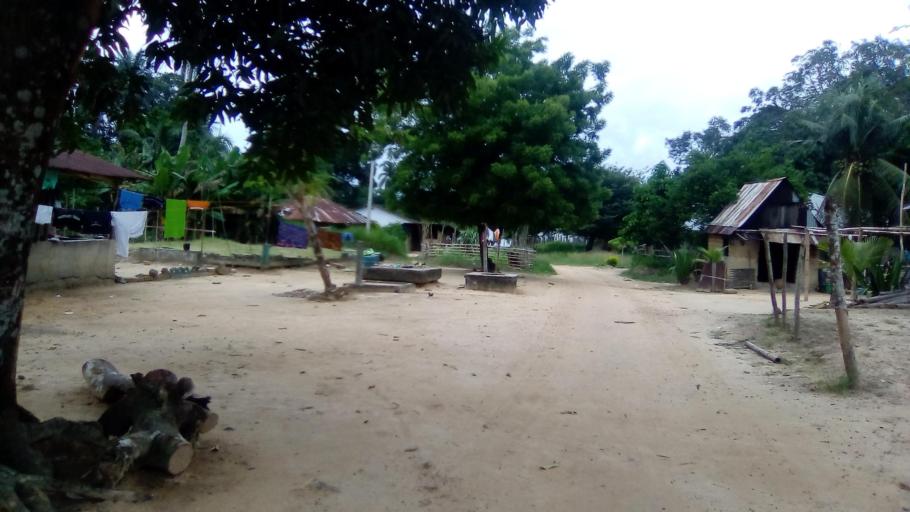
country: SL
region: Southern Province
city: Pujehun
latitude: 7.3626
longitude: -11.7094
